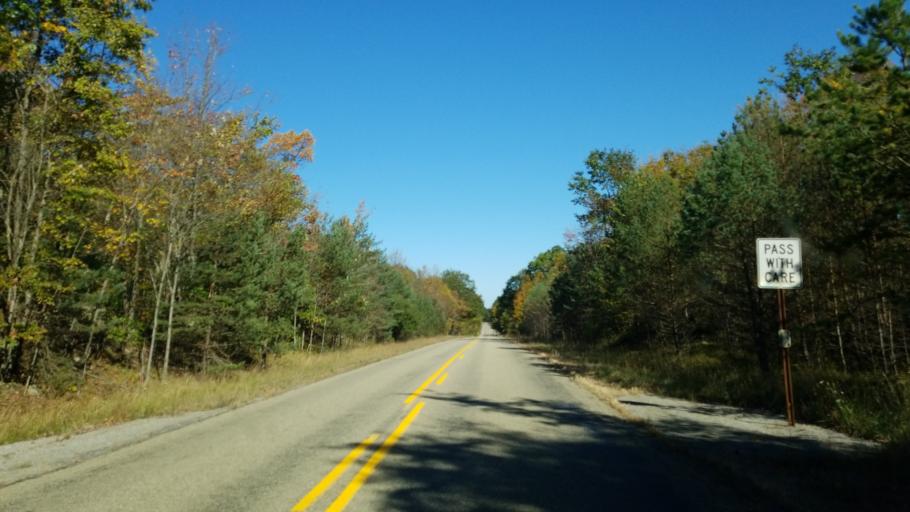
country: US
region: Pennsylvania
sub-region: Clearfield County
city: Shiloh
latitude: 41.2587
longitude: -78.3122
